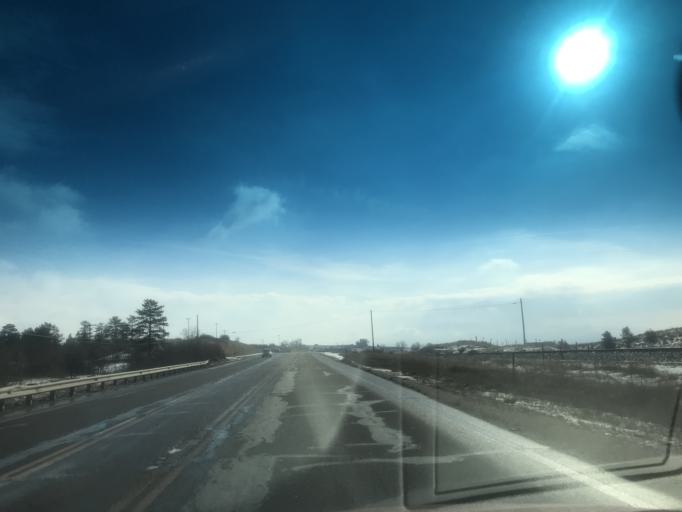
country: US
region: Colorado
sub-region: Douglas County
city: Castle Pines
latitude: 39.4539
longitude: -104.9792
